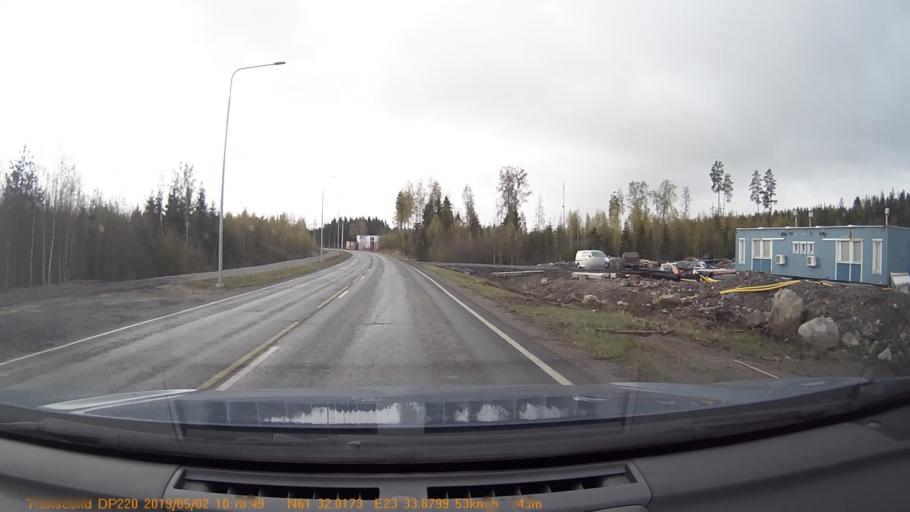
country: FI
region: Pirkanmaa
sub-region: Tampere
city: Yloejaervi
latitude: 61.5337
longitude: 23.5647
